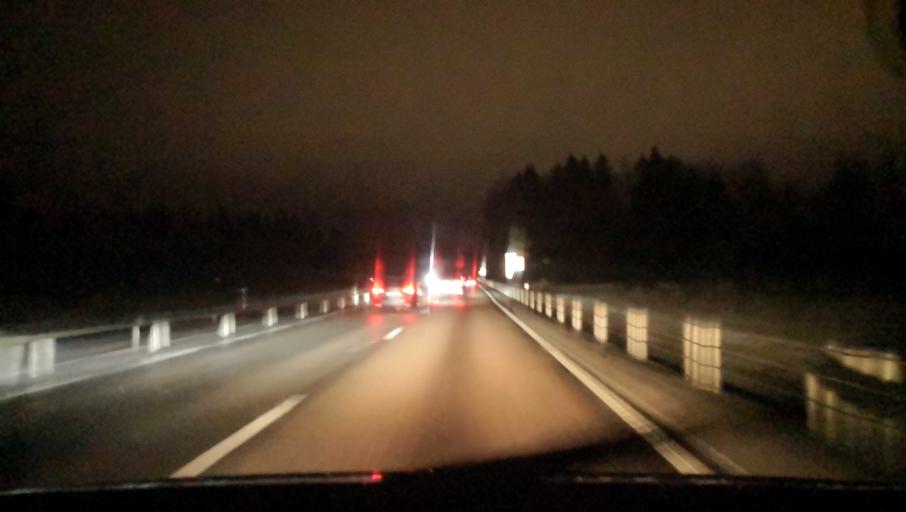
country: SE
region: Uppsala
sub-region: Enkopings Kommun
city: Enkoping
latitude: 59.6763
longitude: 17.0508
